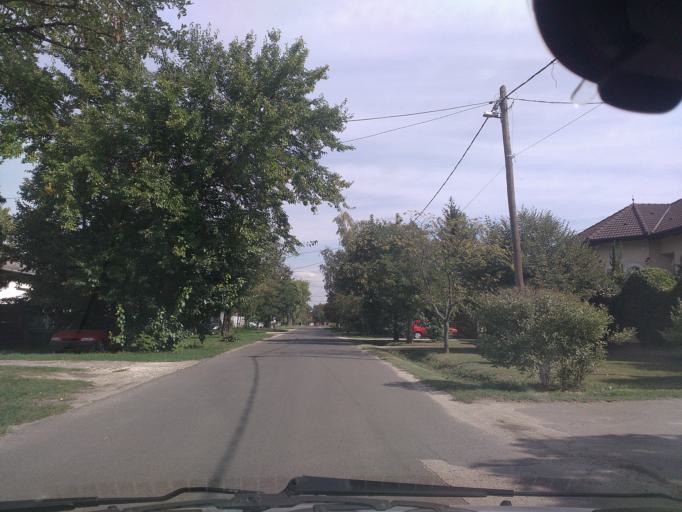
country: HU
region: Pest
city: Gyal
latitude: 47.4223
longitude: 19.2195
